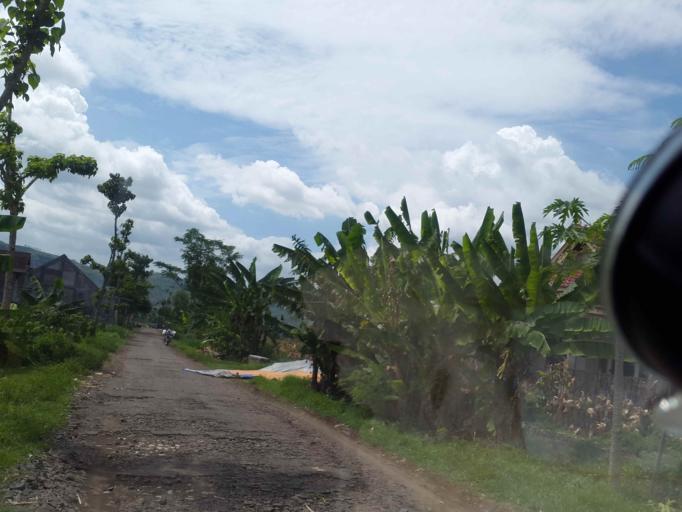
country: ID
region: East Java
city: Tanggung
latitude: -8.1384
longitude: 111.8811
